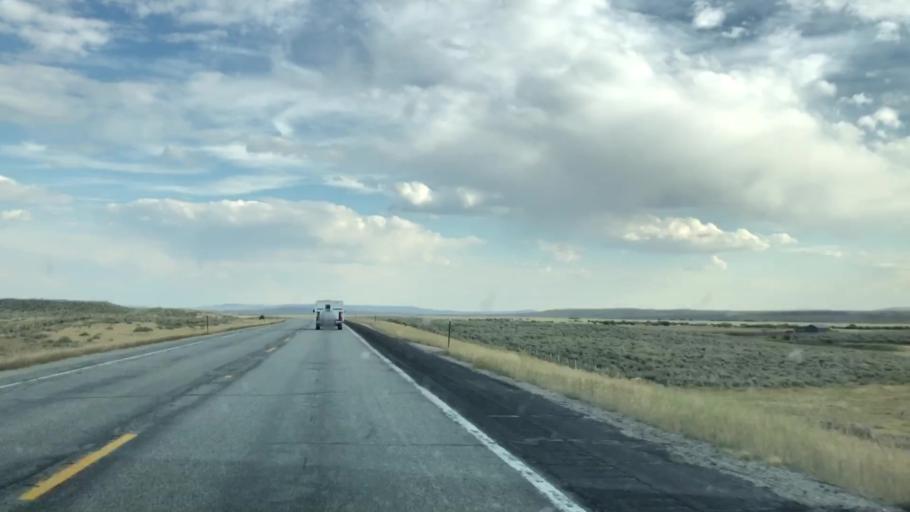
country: US
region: Wyoming
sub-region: Sublette County
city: Pinedale
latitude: 43.0497
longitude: -110.1505
